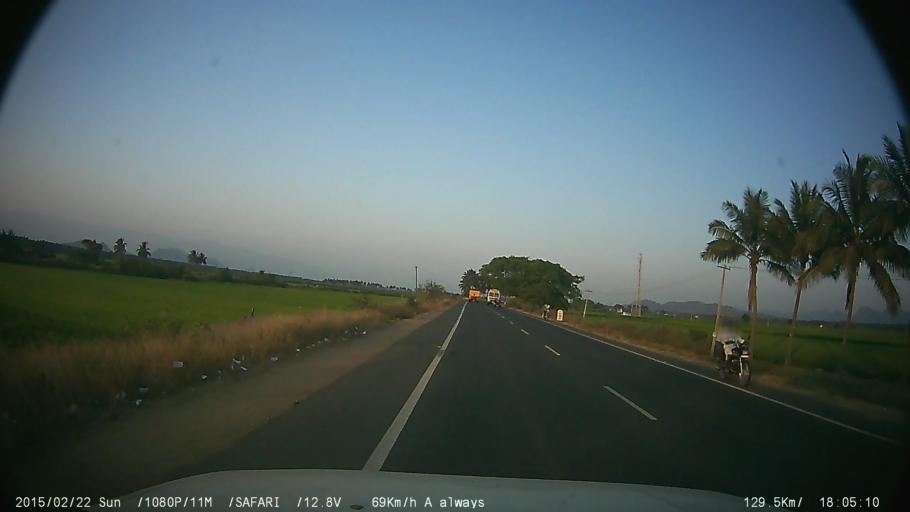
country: IN
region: Tamil Nadu
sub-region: Theni
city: Uttamapalaiyam
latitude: 9.8216
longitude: 77.3545
